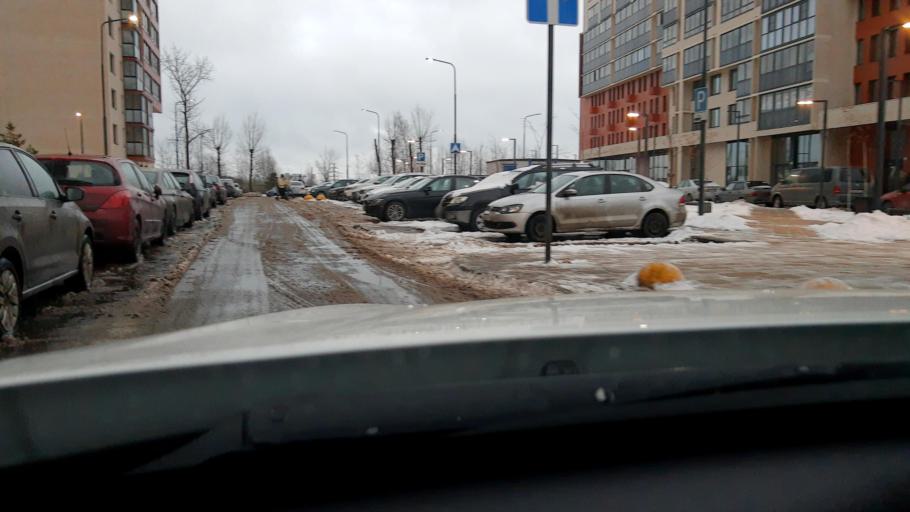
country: RU
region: Moskovskaya
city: Krasnogorsk
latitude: 55.8725
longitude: 37.3155
